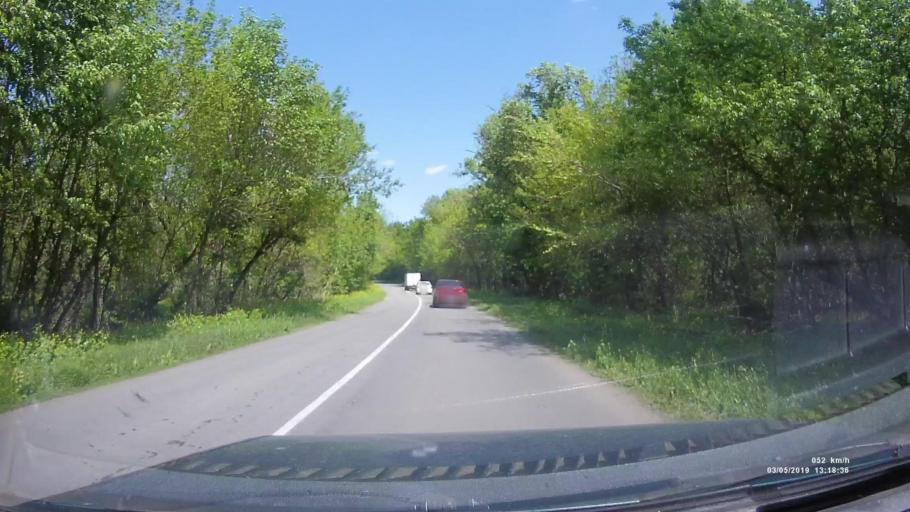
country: RU
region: Rostov
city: Semikarakorsk
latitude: 47.5336
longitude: 40.7496
